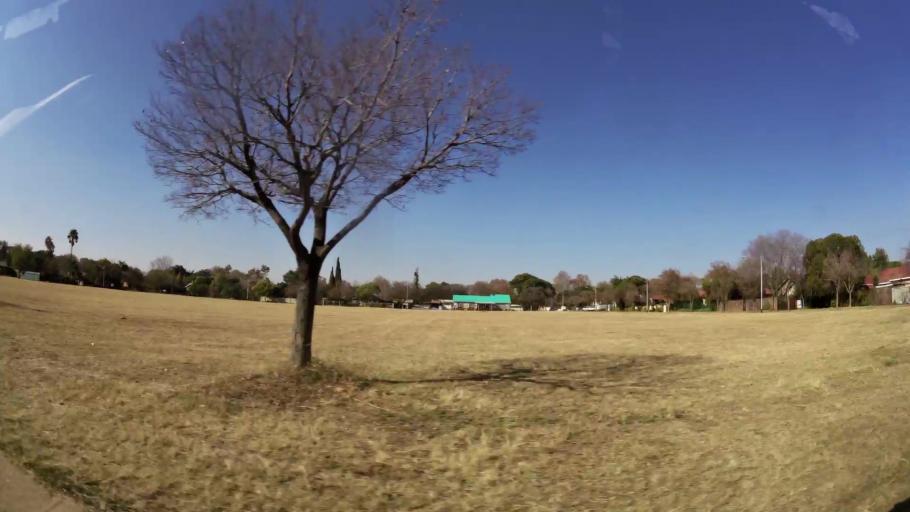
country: ZA
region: Gauteng
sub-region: City of Tshwane Metropolitan Municipality
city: Pretoria
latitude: -25.7277
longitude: 28.2547
